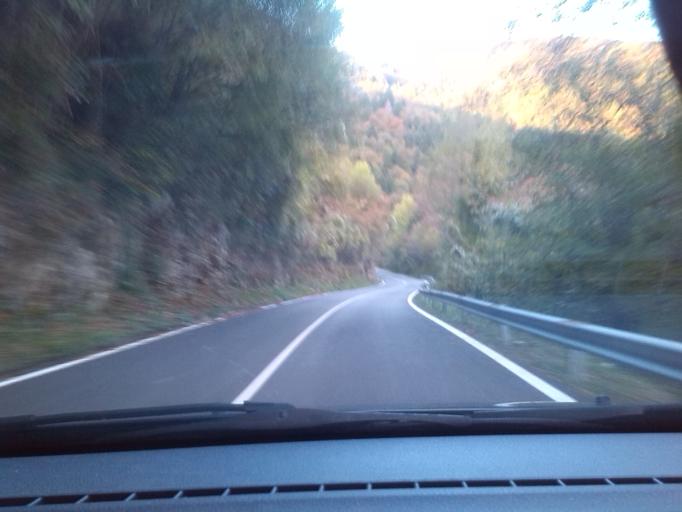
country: IT
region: Friuli Venezia Giulia
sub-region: Provincia di Udine
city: Savogna
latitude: 46.1831
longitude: 13.5555
